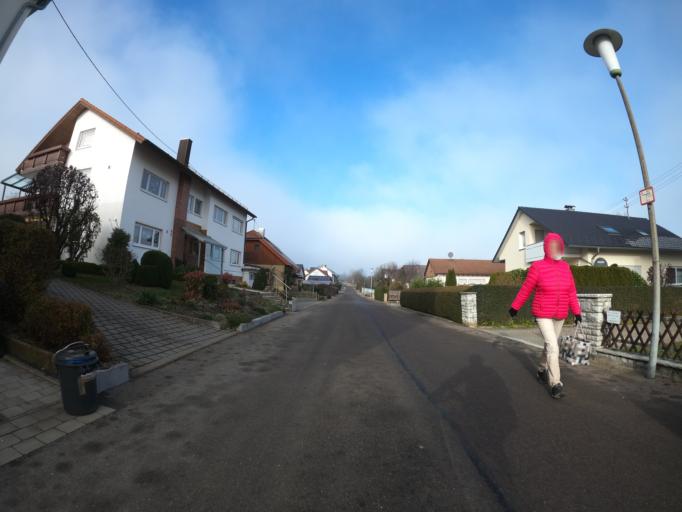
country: DE
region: Baden-Wuerttemberg
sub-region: Regierungsbezirk Stuttgart
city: Bad Uberkingen
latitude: 48.5863
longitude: 9.7595
